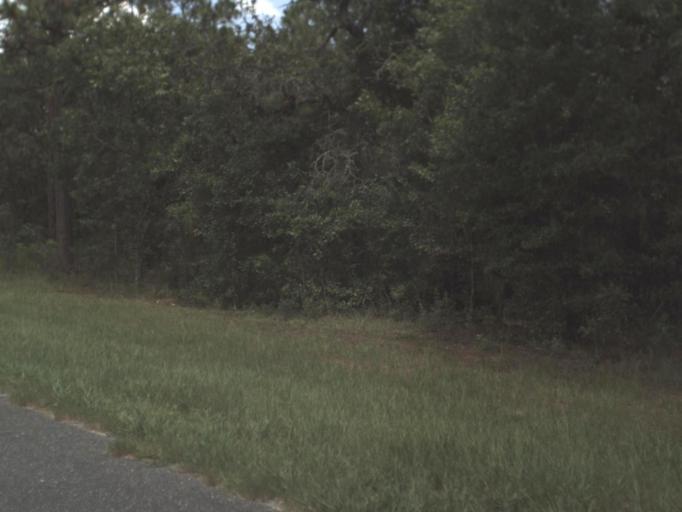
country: US
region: Florida
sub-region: Levy County
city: Williston Highlands
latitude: 29.3328
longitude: -82.5160
